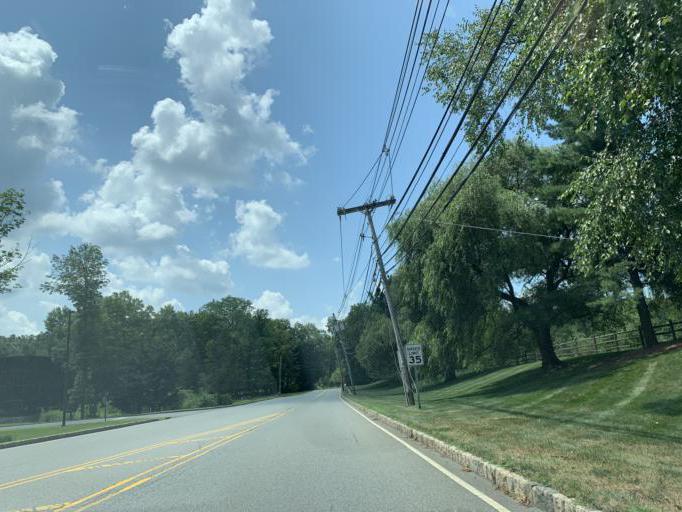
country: US
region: New Jersey
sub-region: Somerset County
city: Bernardsville
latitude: 40.6925
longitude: -74.5787
